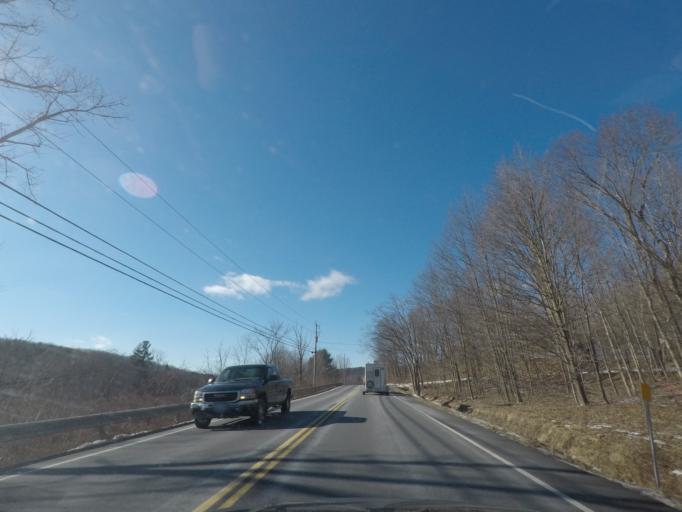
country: US
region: New York
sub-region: Columbia County
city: Chatham
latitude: 42.4180
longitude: -73.4893
